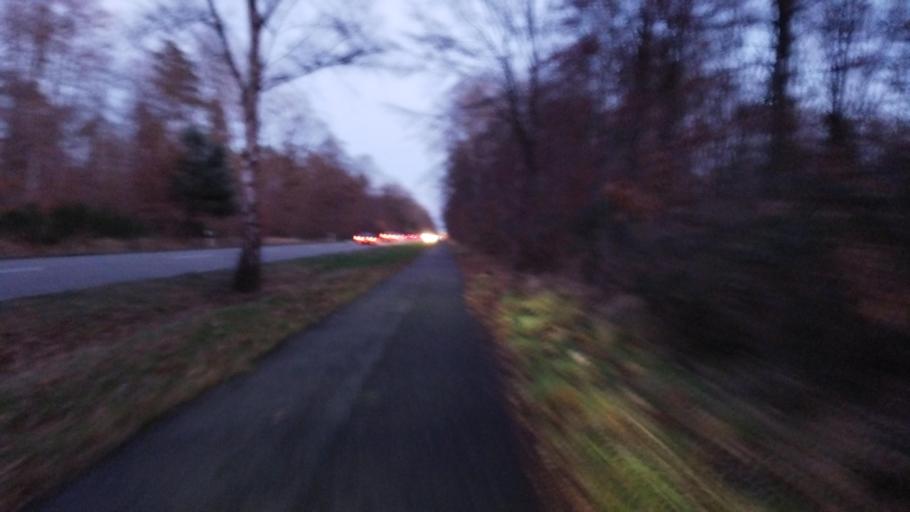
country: DE
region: Rheinland-Pfalz
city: Dudenhofen
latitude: 49.3414
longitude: 8.3946
